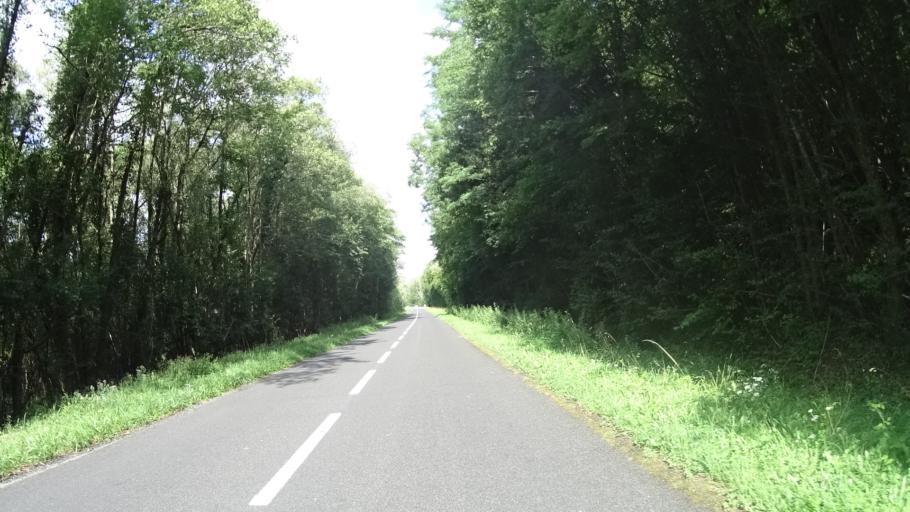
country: FR
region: Lorraine
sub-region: Departement de Meurthe-et-Moselle
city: Gondreville
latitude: 48.6478
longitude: 5.9705
